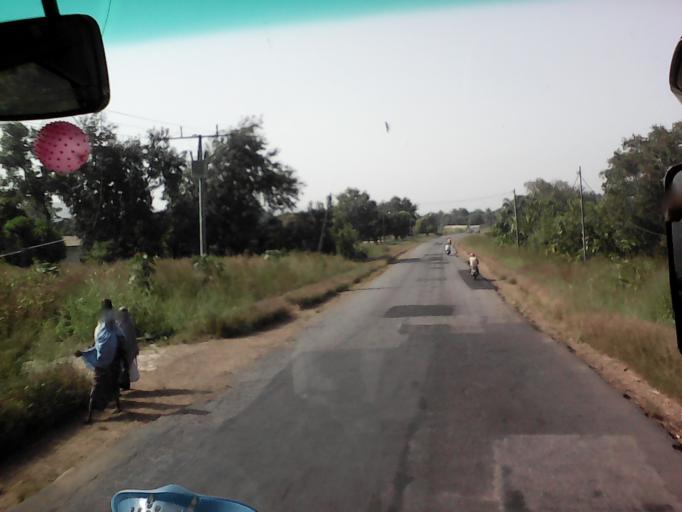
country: TG
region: Centrale
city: Sokode
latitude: 9.1062
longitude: 1.1435
